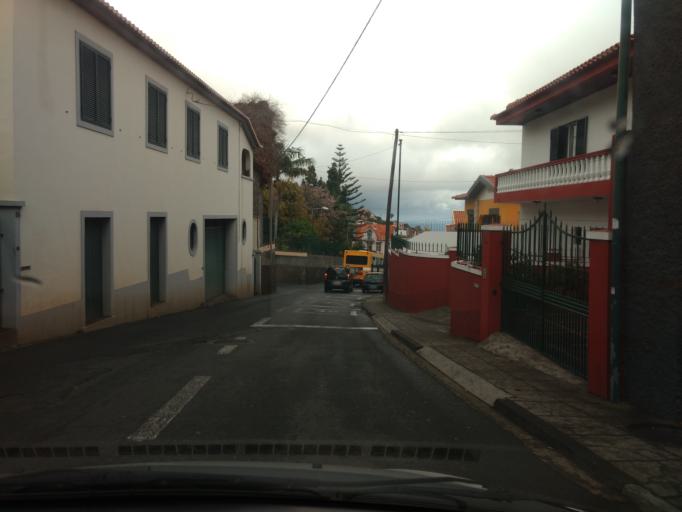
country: PT
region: Madeira
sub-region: Funchal
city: Nossa Senhora do Monte
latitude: 32.6645
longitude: -16.9313
